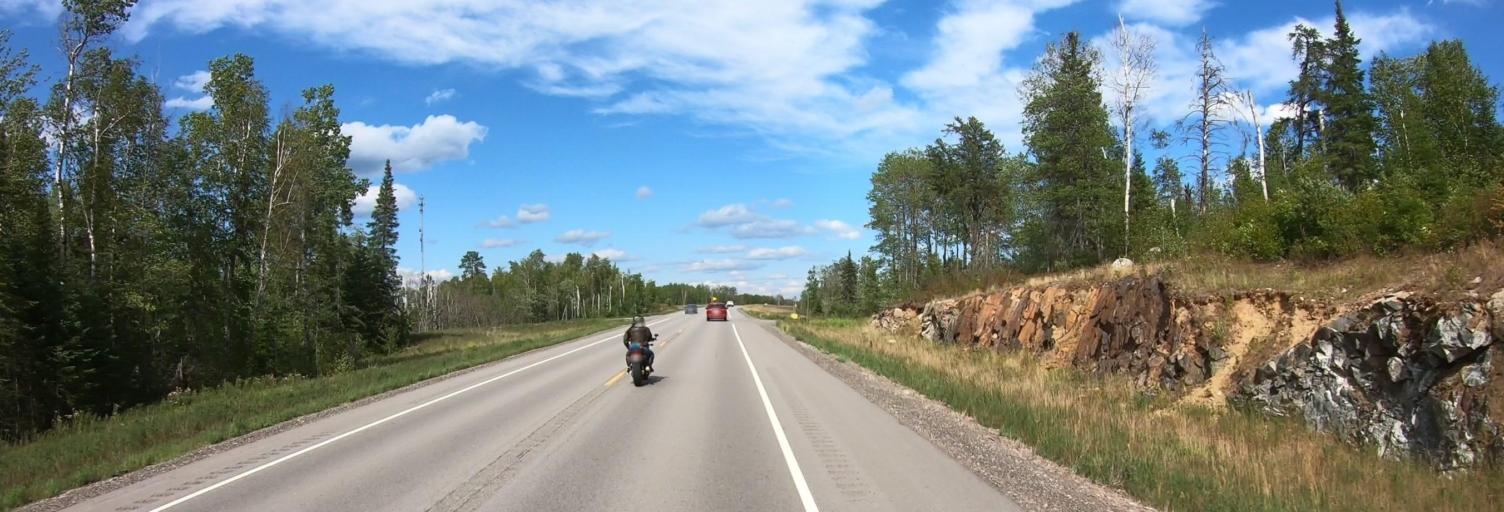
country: US
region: Minnesota
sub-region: Saint Louis County
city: Babbitt
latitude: 47.8368
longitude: -92.1620
